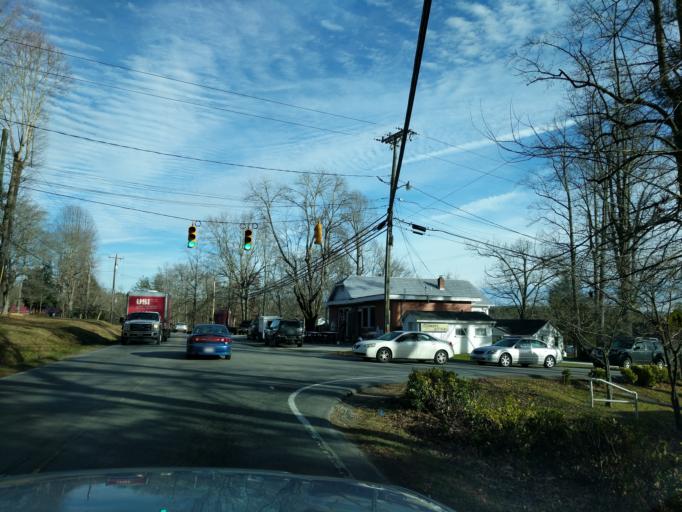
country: US
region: North Carolina
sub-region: Henderson County
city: Fruitland
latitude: 35.3767
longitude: -82.3693
